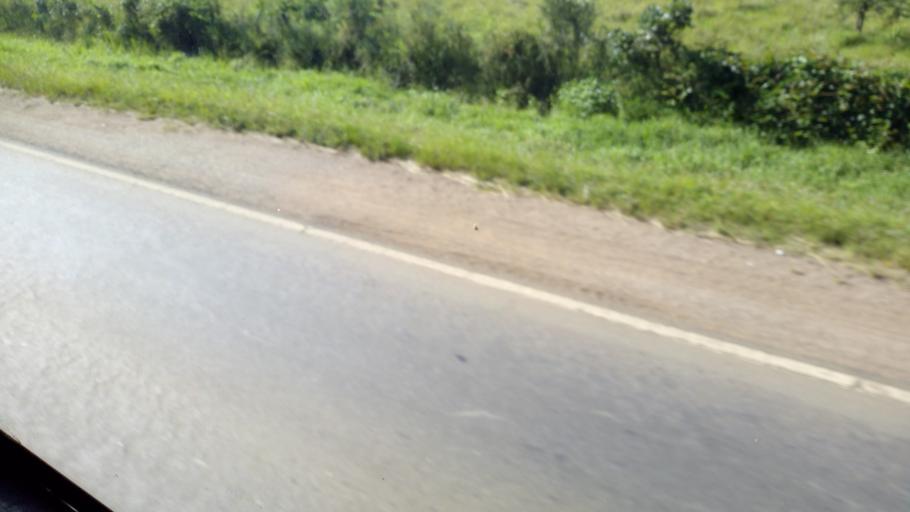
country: UG
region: Central Region
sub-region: Lyantonde District
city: Lyantonde
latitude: -0.4190
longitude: 31.1183
